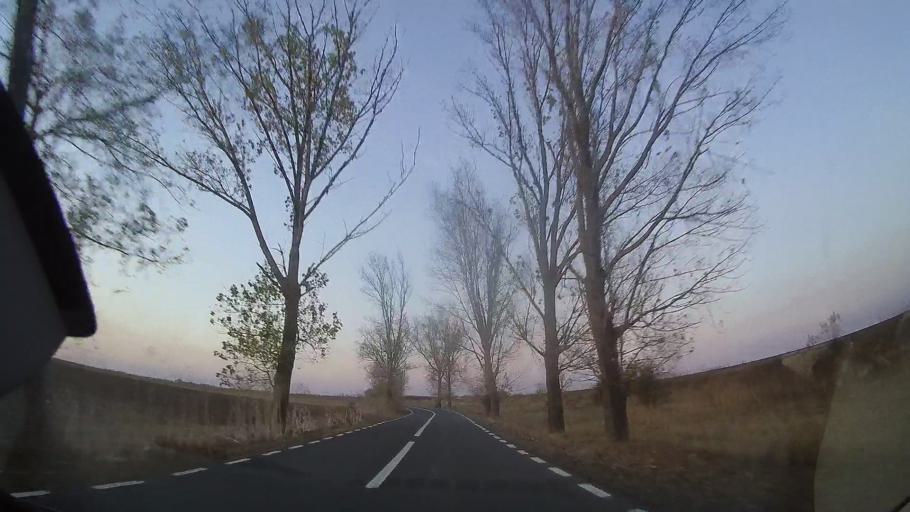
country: RO
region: Constanta
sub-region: Comuna Cobadin
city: Cobadin
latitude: 44.0390
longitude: 28.2577
